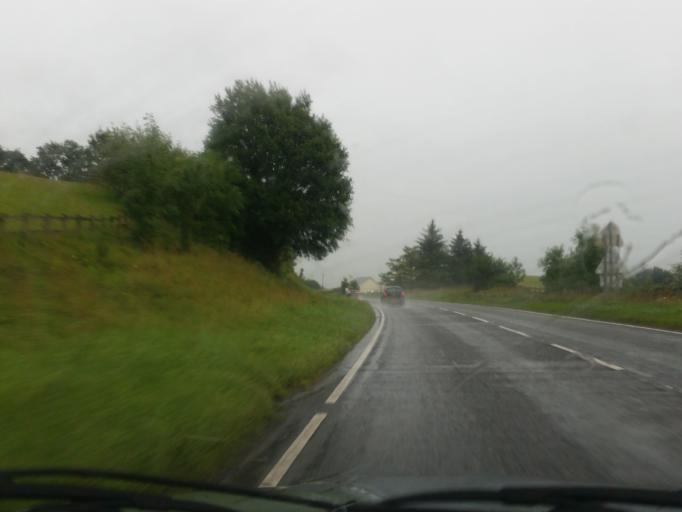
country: GB
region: Northern Ireland
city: Lisnaskea
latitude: 54.2764
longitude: -7.4669
